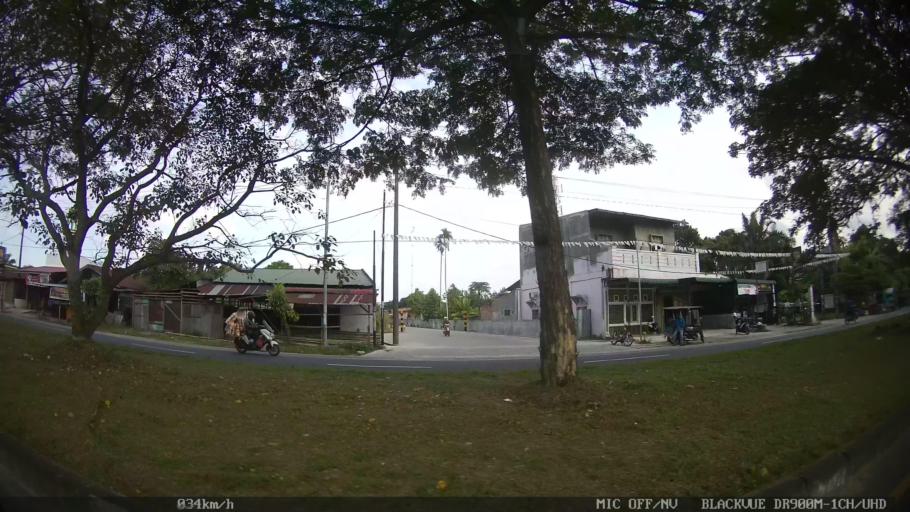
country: ID
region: North Sumatra
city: Percut
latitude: 3.5646
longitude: 98.7933
